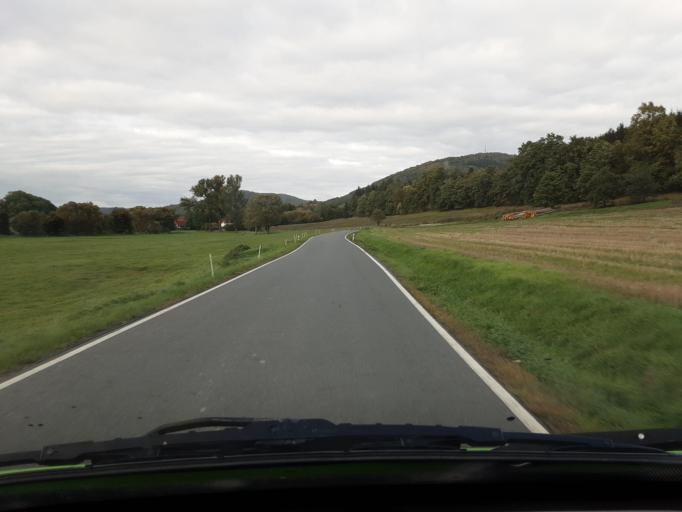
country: CZ
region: Plzensky
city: Janovice nad Uhlavou
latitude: 49.4182
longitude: 13.1769
